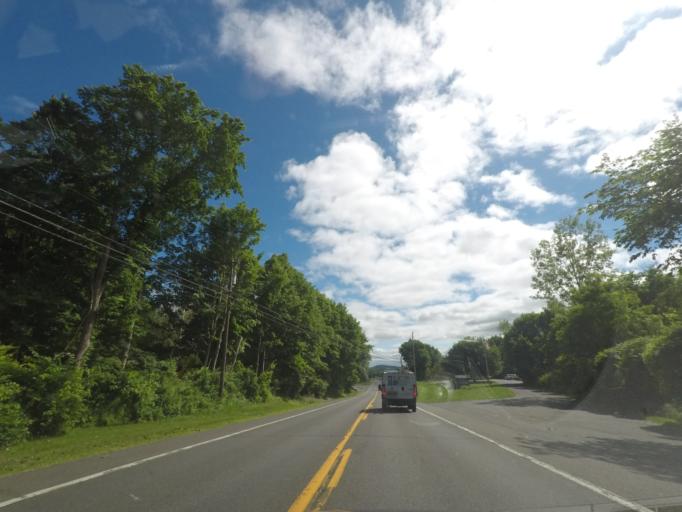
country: US
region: New York
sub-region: Dutchess County
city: Pine Plains
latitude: 42.1091
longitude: -73.5377
